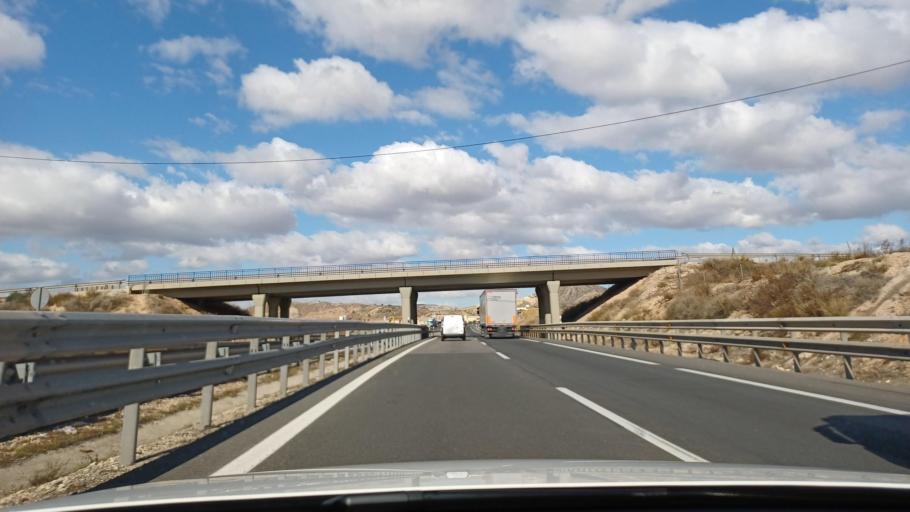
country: ES
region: Valencia
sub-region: Provincia de Alicante
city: Novelda
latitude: 38.4112
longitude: -0.7788
